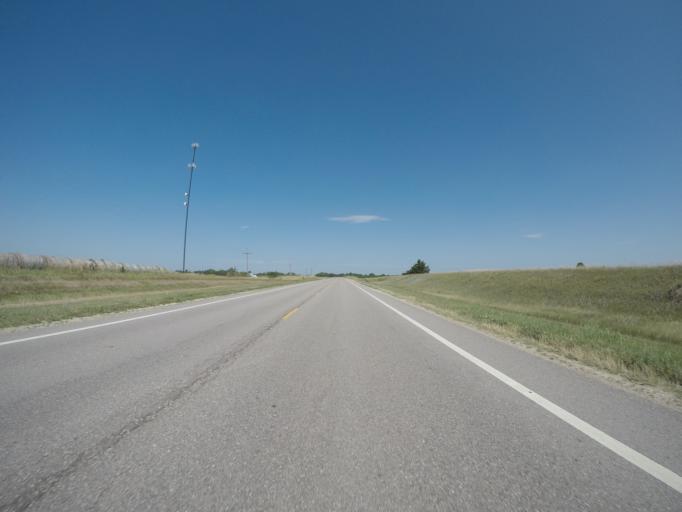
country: US
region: Kansas
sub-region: Cloud County
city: Concordia
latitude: 39.3743
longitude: -97.8457
